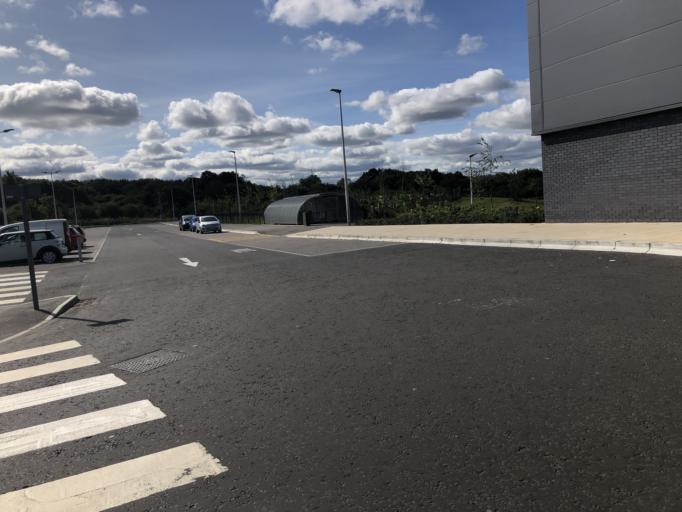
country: GB
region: Scotland
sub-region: Midlothian
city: Dalkeith
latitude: 55.8741
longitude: -3.0489
